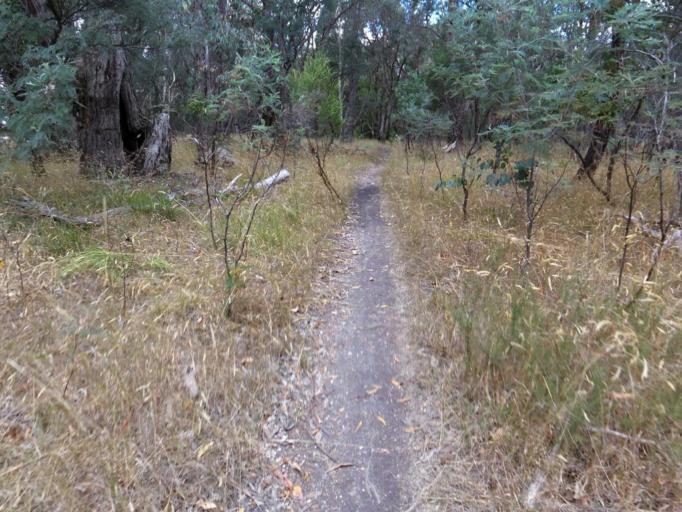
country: AU
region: Victoria
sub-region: Melton
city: Melton West
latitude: -37.4816
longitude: 144.5404
